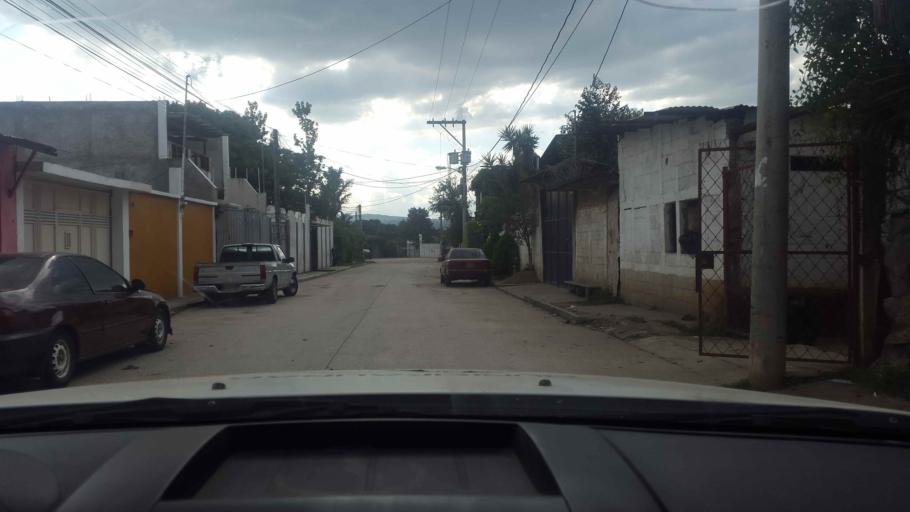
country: GT
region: Guatemala
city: Petapa
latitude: 14.5219
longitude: -90.5377
